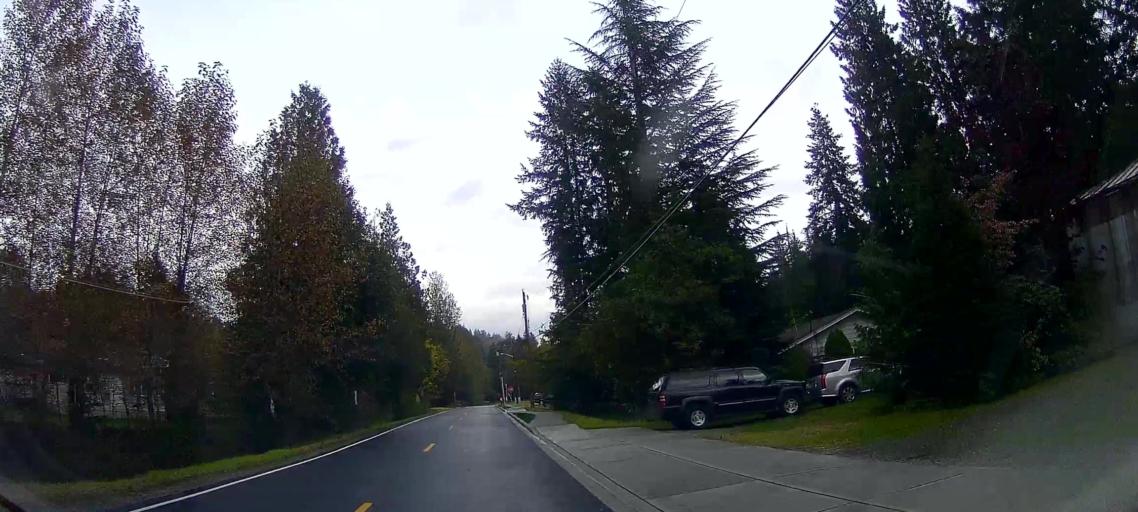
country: US
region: Washington
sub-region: Snohomish County
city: Darrington
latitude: 48.5346
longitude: -121.7607
